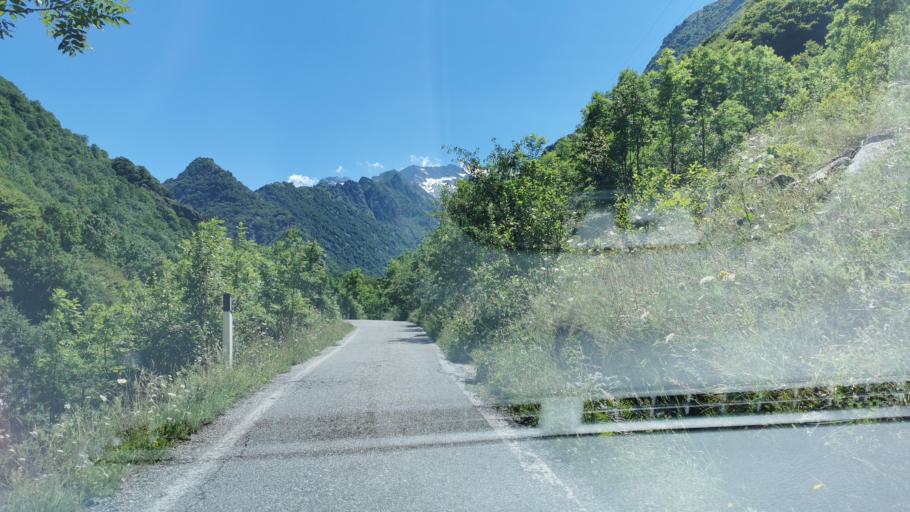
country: IT
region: Piedmont
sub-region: Provincia di Cuneo
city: Entracque
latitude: 44.1871
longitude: 7.3836
